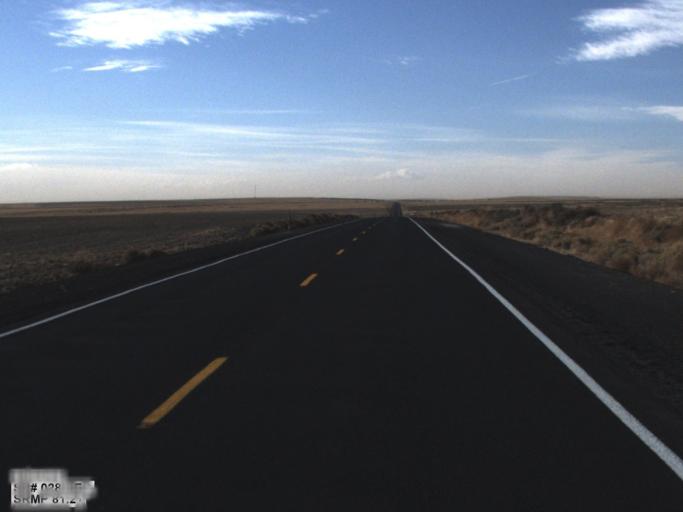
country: US
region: Washington
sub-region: Grant County
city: Warden
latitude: 47.3513
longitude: -118.9382
